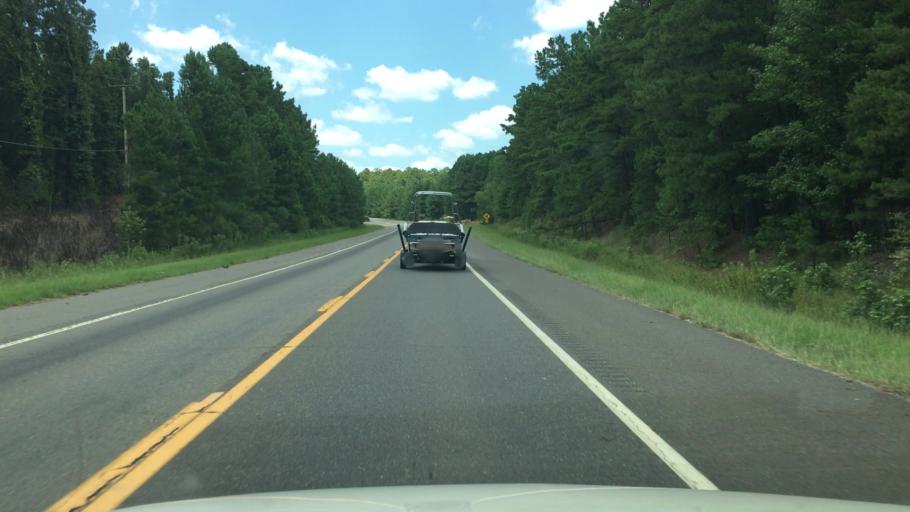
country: US
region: Arkansas
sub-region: Clark County
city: Arkadelphia
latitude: 34.2071
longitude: -93.0792
